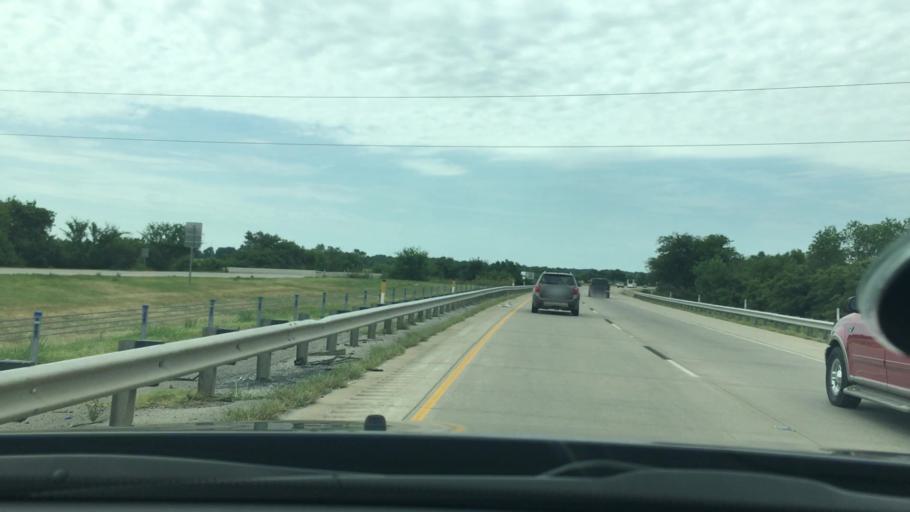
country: US
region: Oklahoma
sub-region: Murray County
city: Davis
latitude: 34.3485
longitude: -97.1480
